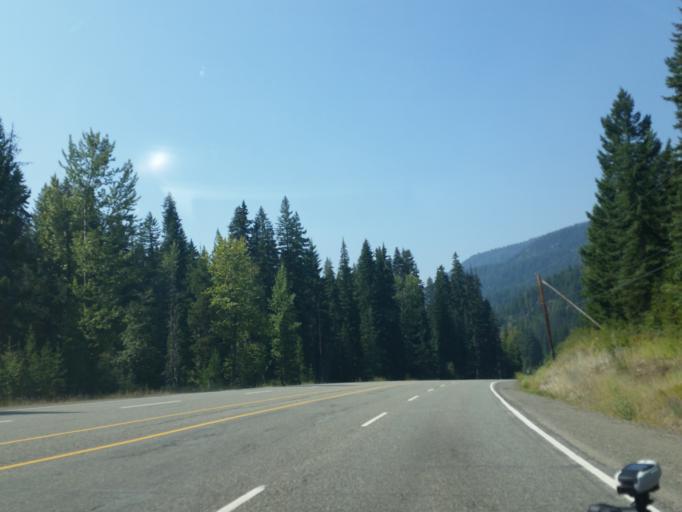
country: CA
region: British Columbia
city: Princeton
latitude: 49.1128
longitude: -120.6483
